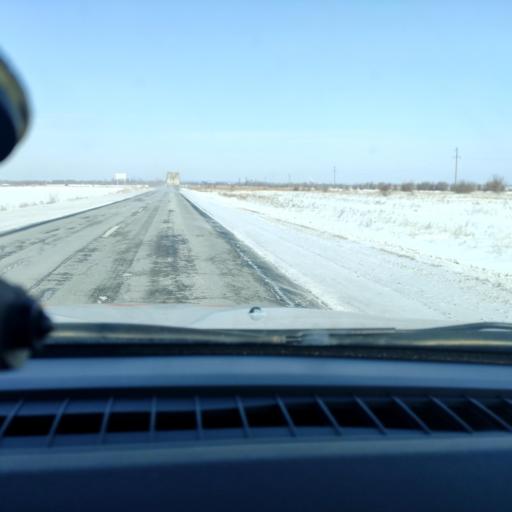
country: RU
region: Samara
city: Smyshlyayevka
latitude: 53.1590
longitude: 50.4569
